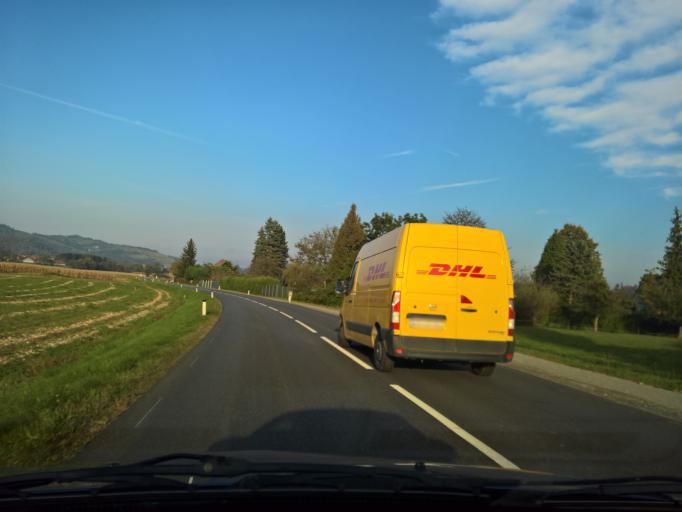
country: AT
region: Styria
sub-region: Politischer Bezirk Leibnitz
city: Heimschuh
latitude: 46.7532
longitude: 15.4780
